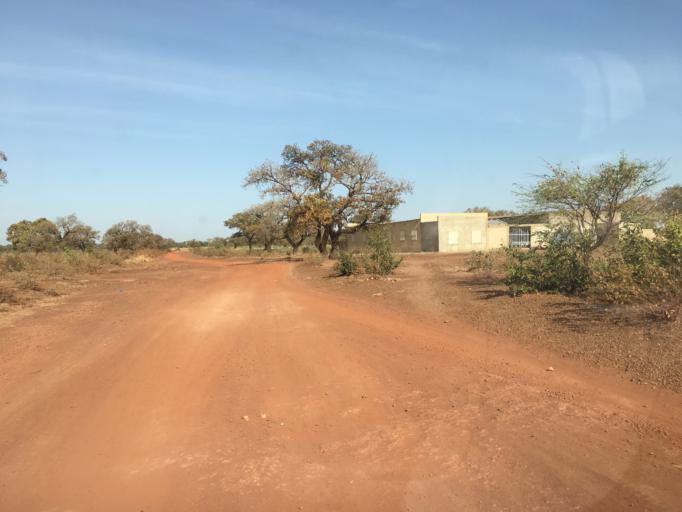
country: BF
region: Plateau-Central
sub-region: Province du Kourweogo
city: Bousse
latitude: 12.5651
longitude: -1.9084
